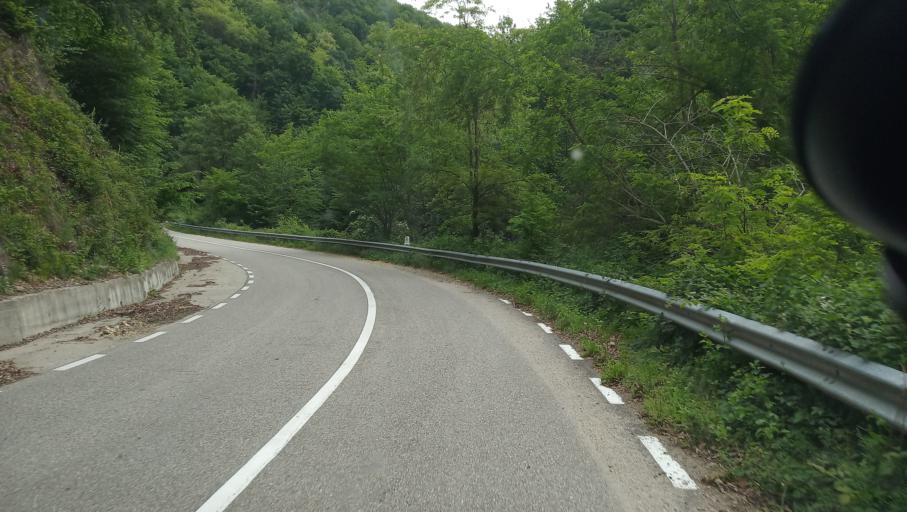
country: RO
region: Caras-Severin
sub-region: Comuna Slatina-Timis
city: Slatina-Timis
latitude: 45.2580
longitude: 22.2532
